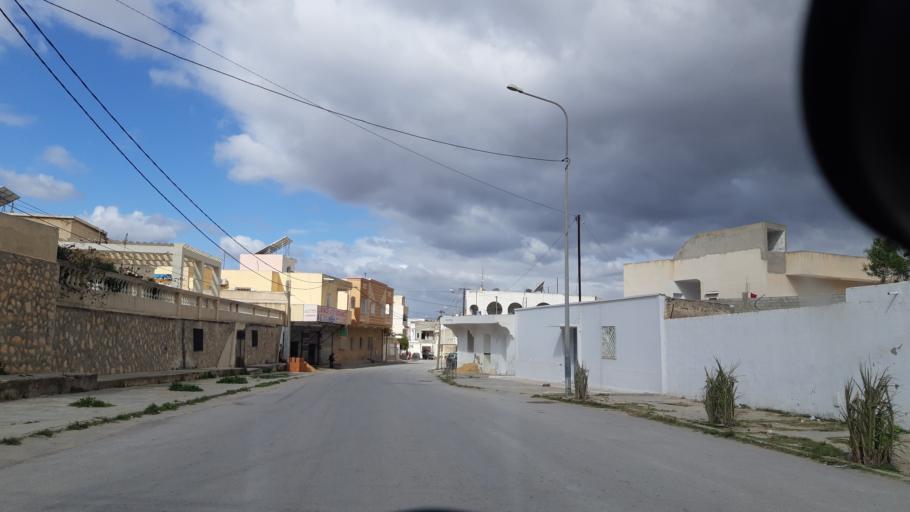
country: TN
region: Susah
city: Akouda
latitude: 35.8721
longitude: 10.5241
